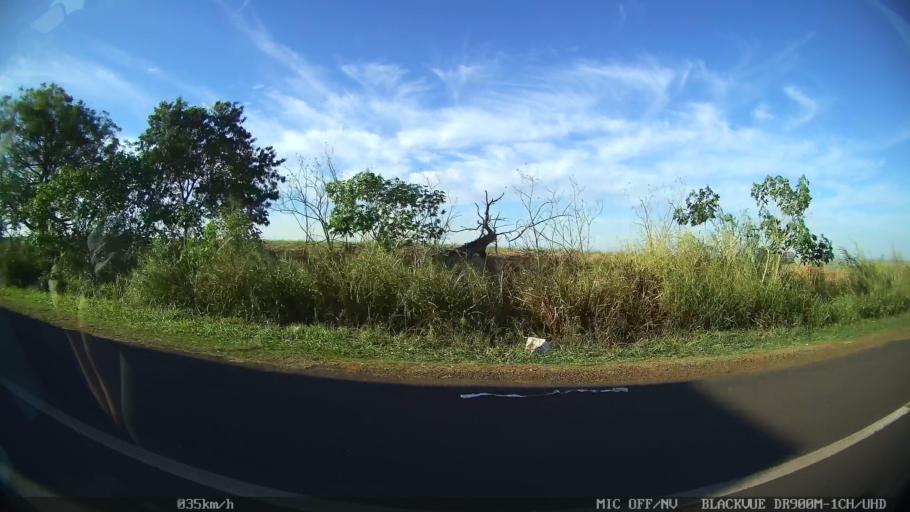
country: BR
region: Sao Paulo
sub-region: Americo Brasiliense
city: Americo Brasiliense
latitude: -21.7726
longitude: -48.1035
